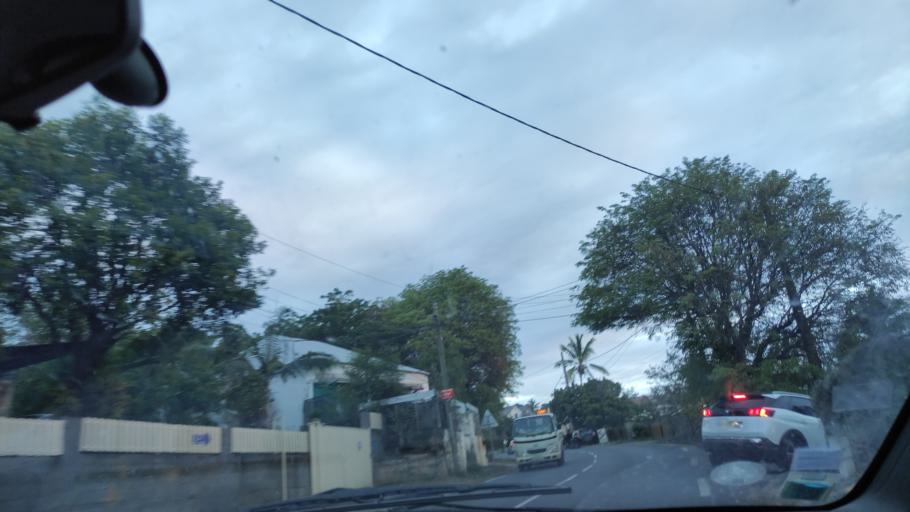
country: RE
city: Piton Saint-Leu
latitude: -21.2105
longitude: 55.3007
